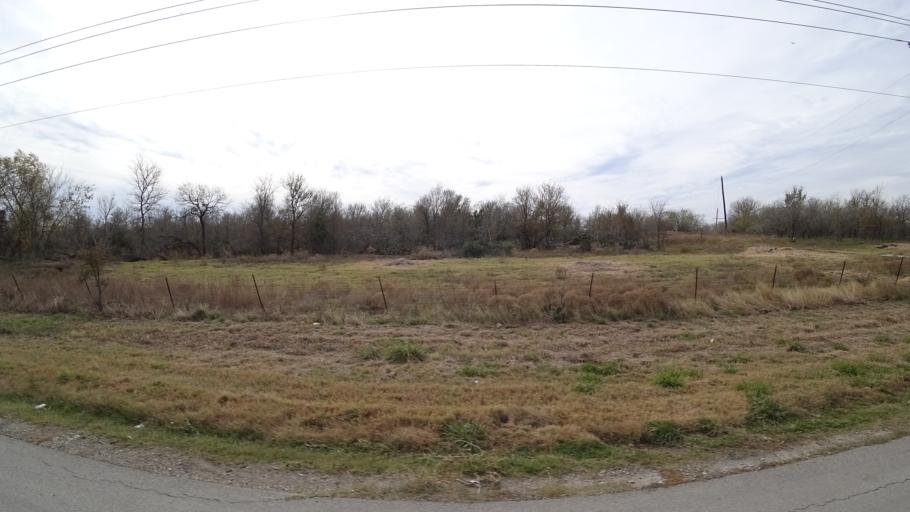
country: US
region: Texas
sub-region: Travis County
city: Garfield
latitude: 30.1614
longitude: -97.6062
